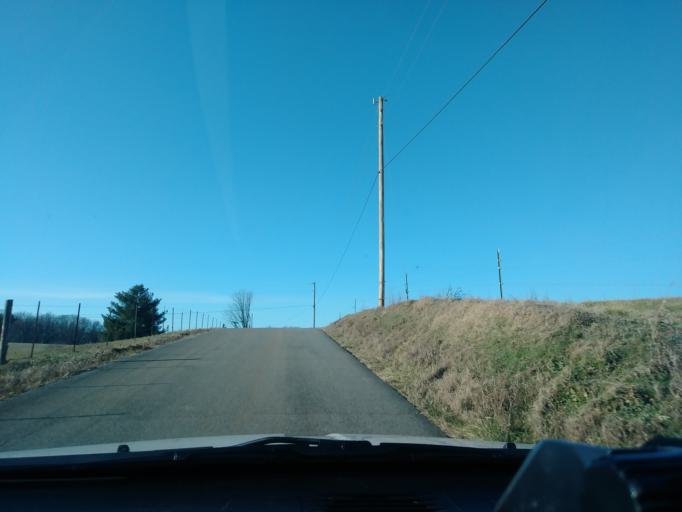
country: US
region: Tennessee
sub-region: Greene County
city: Greeneville
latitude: 36.0795
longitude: -82.9056
